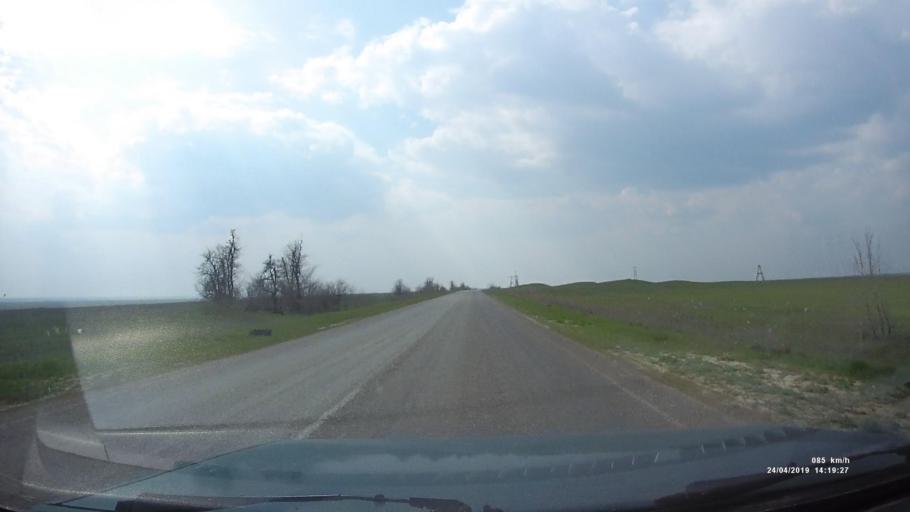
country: RU
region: Kalmykiya
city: Arshan'
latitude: 46.3055
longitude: 44.1754
